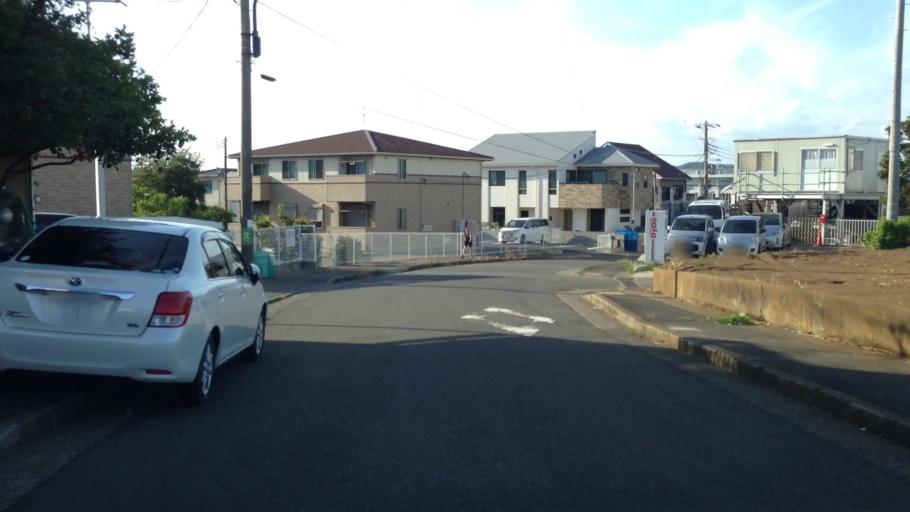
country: JP
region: Kanagawa
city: Miura
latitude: 35.2034
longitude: 139.6154
